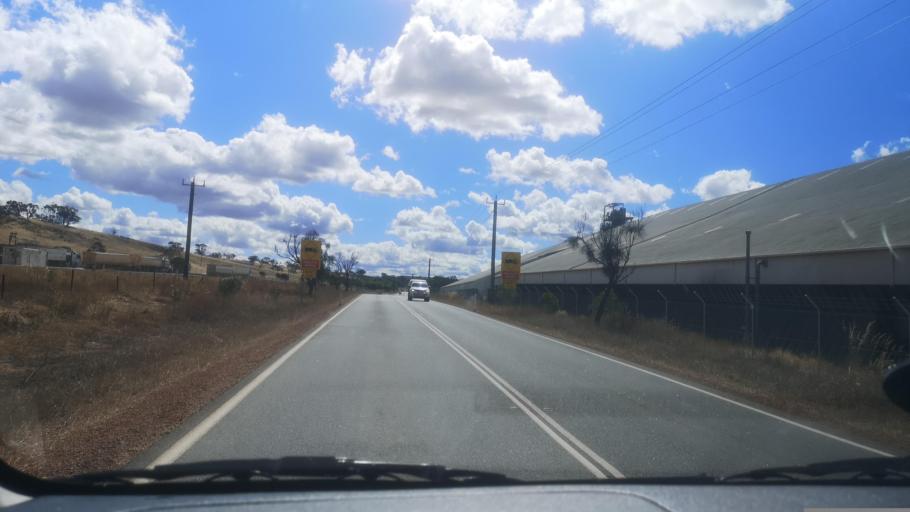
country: AU
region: Western Australia
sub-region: Northam
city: Northam
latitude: -31.6425
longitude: 116.6362
